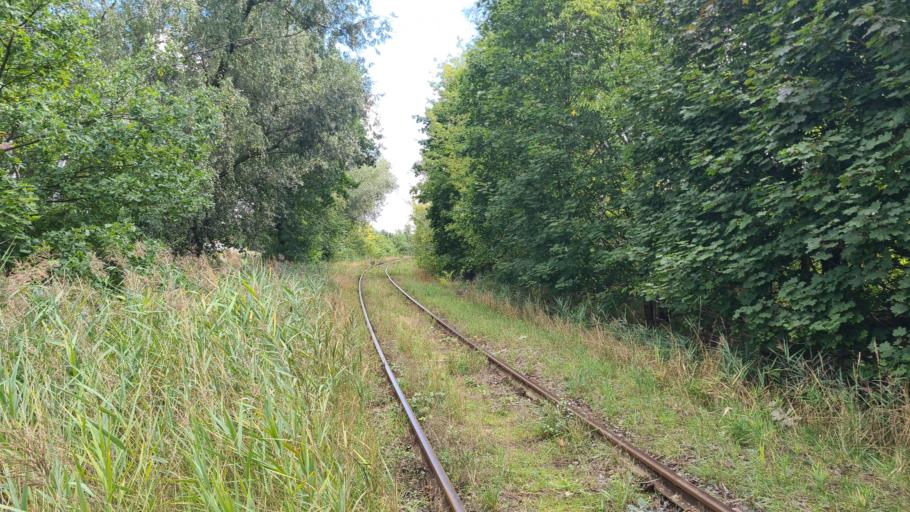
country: DE
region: Brandenburg
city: Finsterwalde
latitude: 51.6392
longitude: 13.7240
